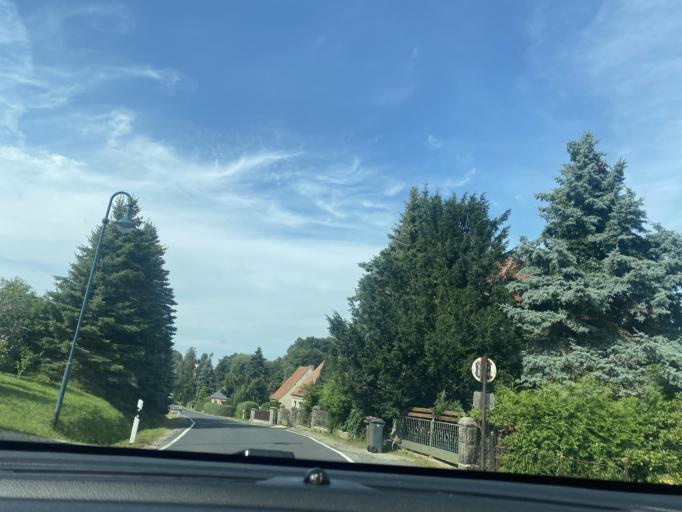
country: DE
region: Saxony
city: Sohland am Rotstein
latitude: 51.1114
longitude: 14.7827
